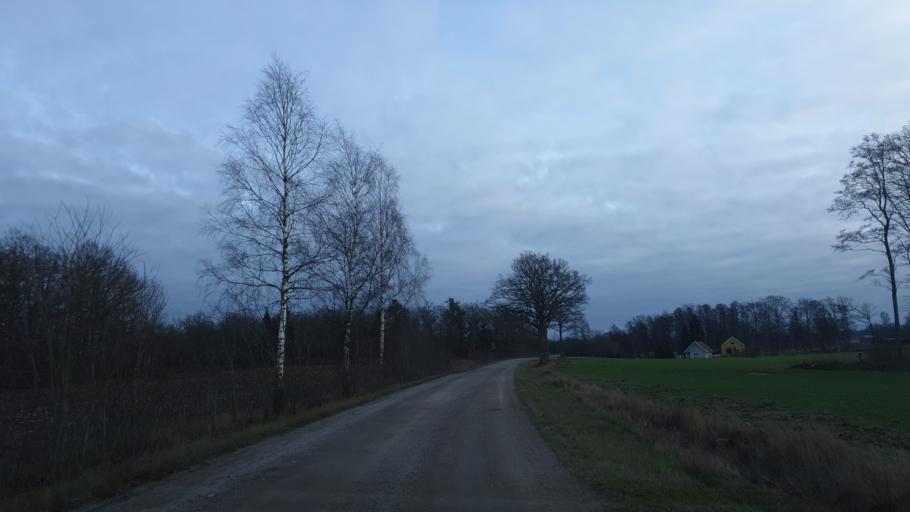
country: SE
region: Kalmar
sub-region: Torsas Kommun
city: Torsas
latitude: 56.3114
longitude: 16.0375
